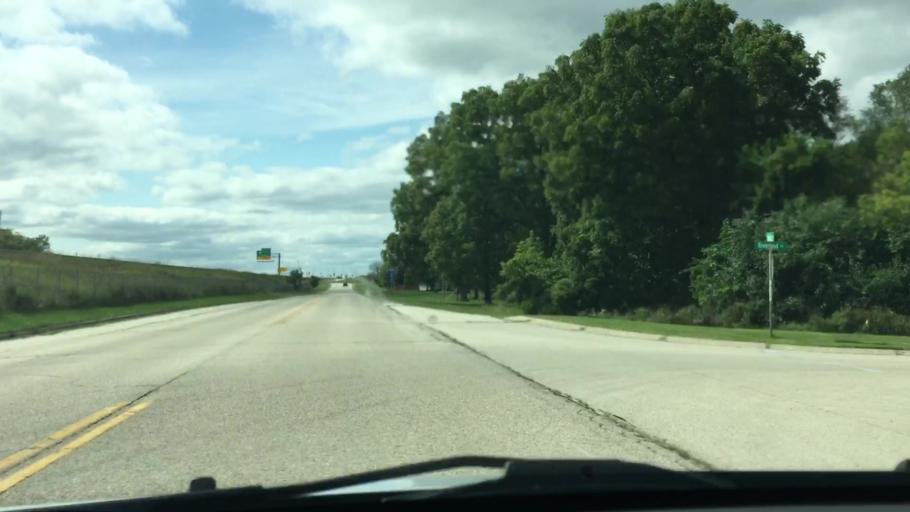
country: US
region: Wisconsin
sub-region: Waukesha County
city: Pewaukee
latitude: 43.0507
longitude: -88.2952
